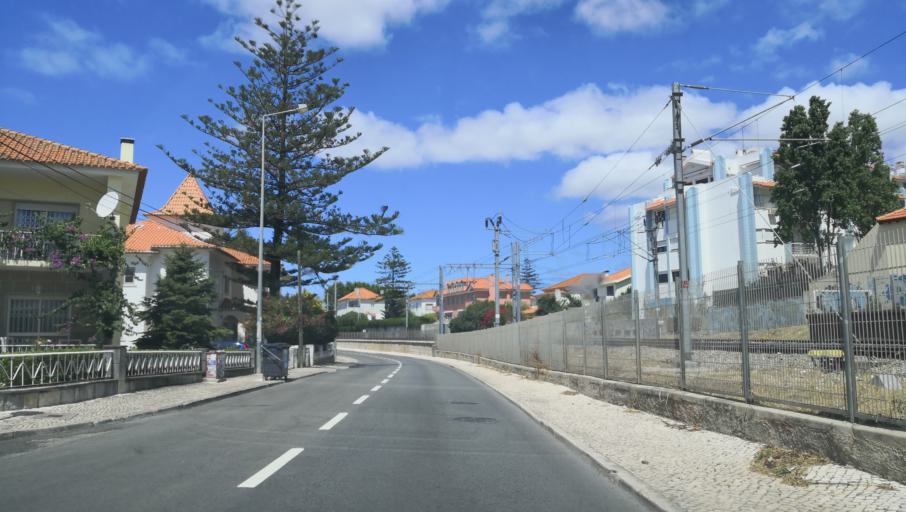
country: PT
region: Lisbon
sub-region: Cascais
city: Parede
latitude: 38.6901
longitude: -9.3577
